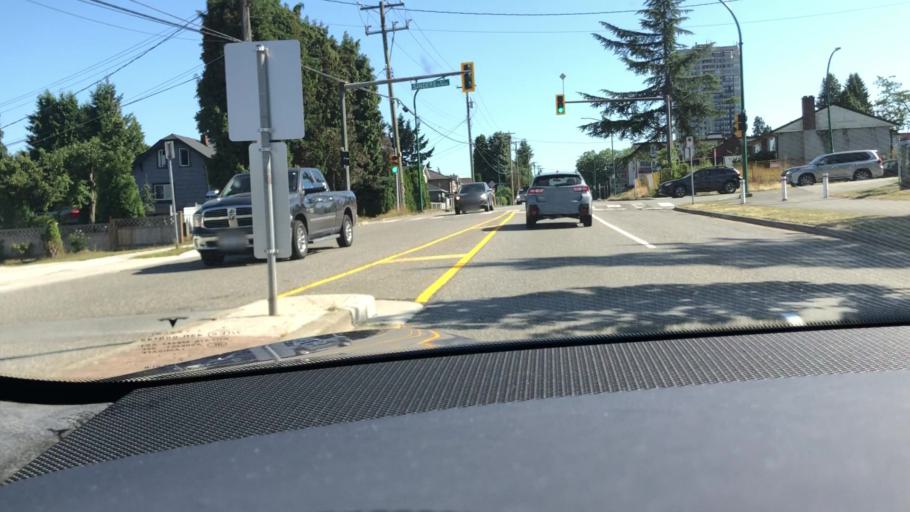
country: CA
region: British Columbia
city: Burnaby
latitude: 49.2283
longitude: -122.9890
